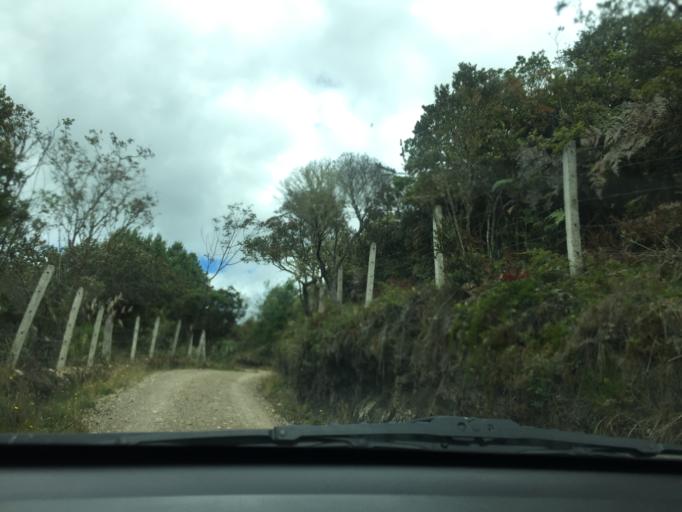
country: CO
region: Cundinamarca
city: Tocancipa
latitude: 4.9607
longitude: -73.8817
